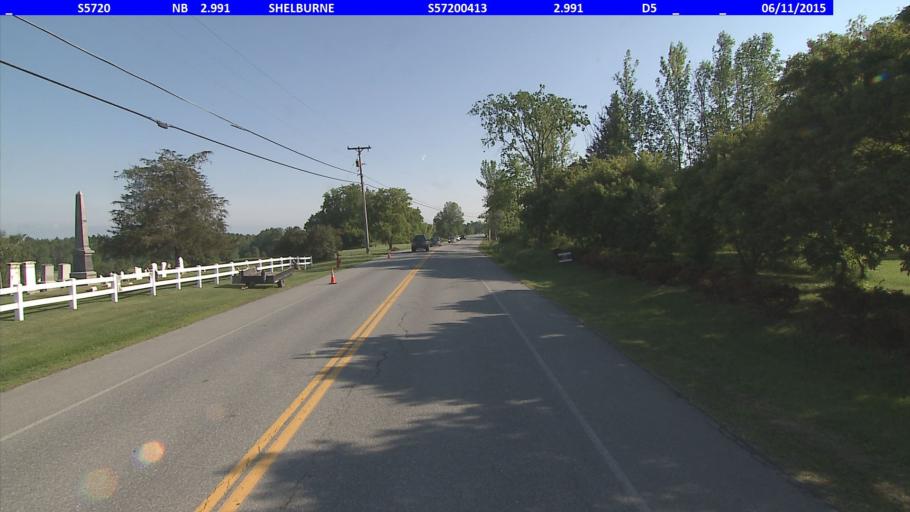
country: US
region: Vermont
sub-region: Chittenden County
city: South Burlington
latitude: 44.4106
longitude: -73.1977
